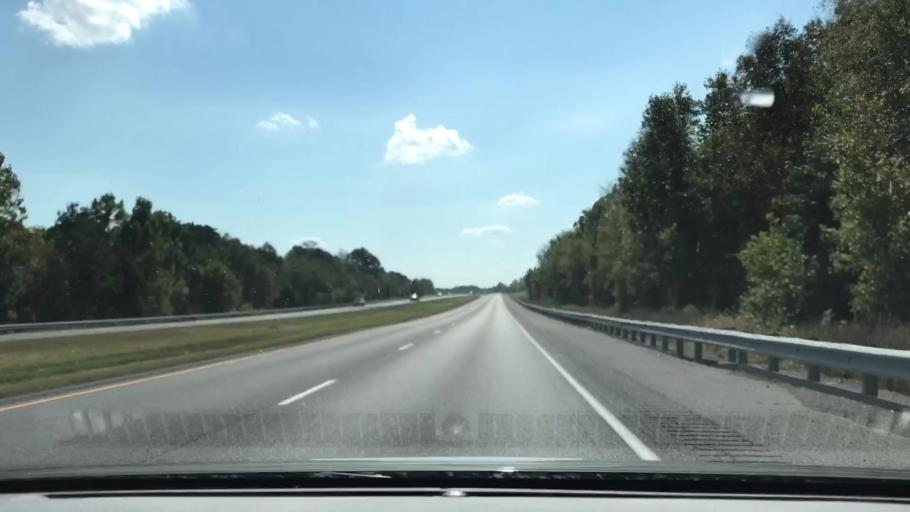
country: US
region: Kentucky
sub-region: Marshall County
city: Benton
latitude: 36.8040
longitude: -88.3432
